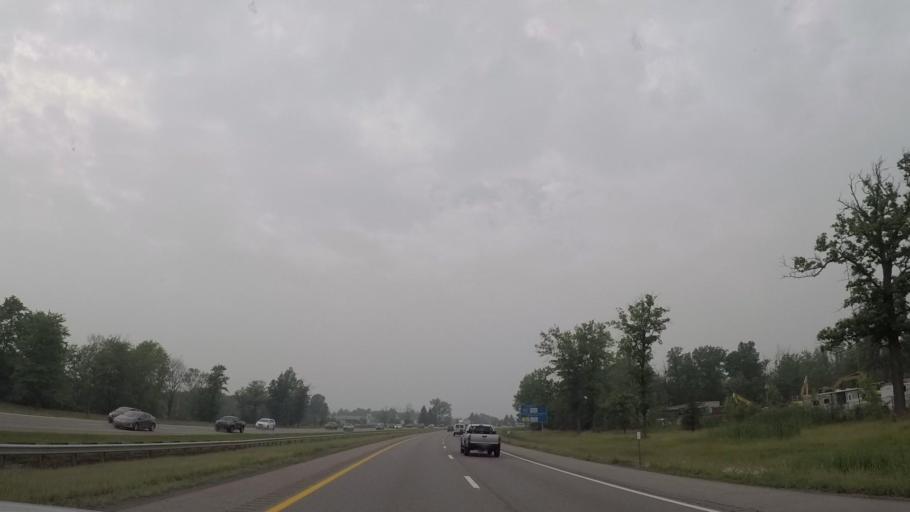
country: US
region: New York
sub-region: Erie County
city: Grandyle Village
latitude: 43.0131
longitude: -78.9670
